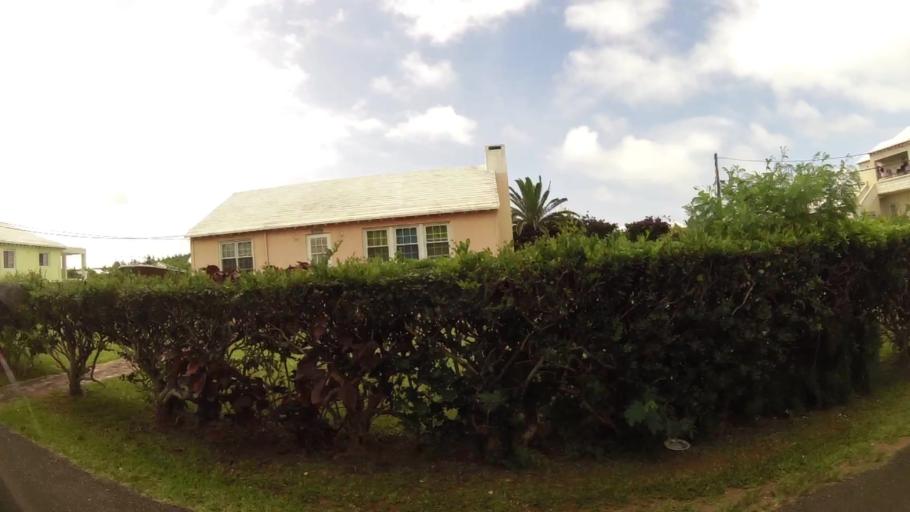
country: BM
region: Saint George
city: Saint George
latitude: 32.3707
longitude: -64.6545
